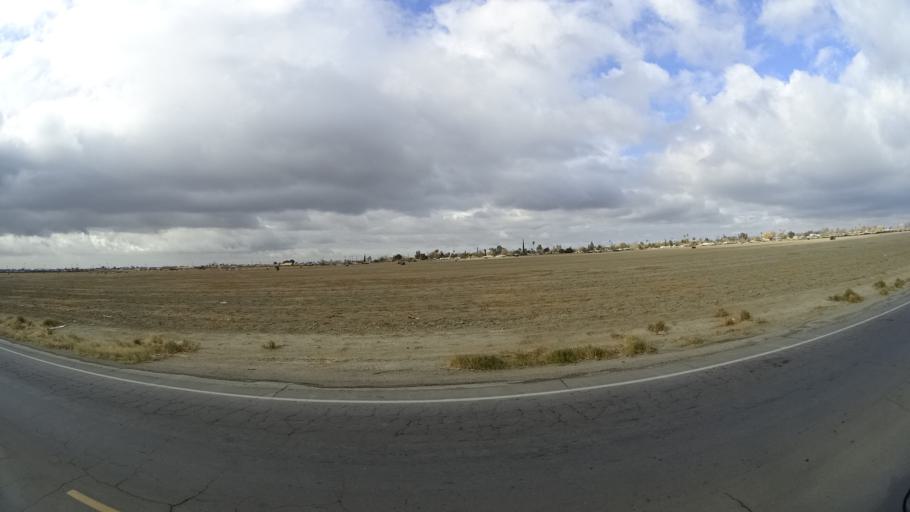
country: US
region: California
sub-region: Kern County
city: Greenfield
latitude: 35.3005
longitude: -118.9853
